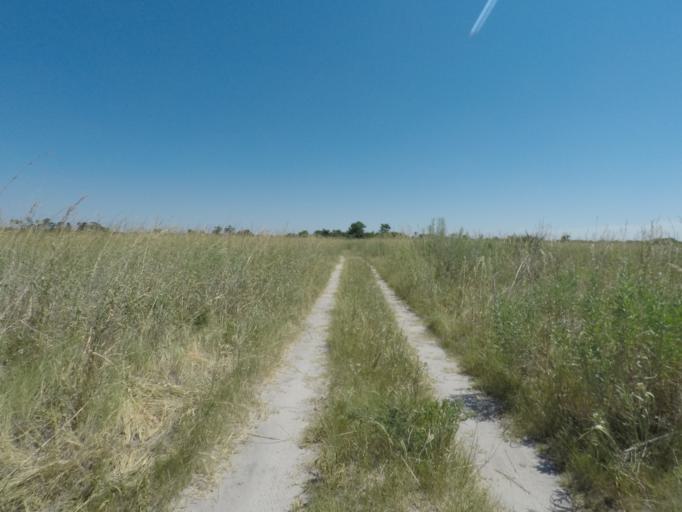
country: BW
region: North West
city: Maun
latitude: -19.4858
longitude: 23.5296
